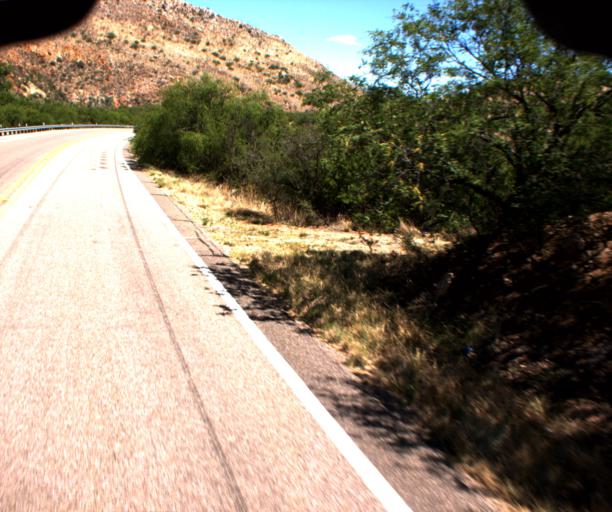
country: US
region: Arizona
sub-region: Santa Cruz County
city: Rio Rico
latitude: 31.5027
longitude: -110.8090
